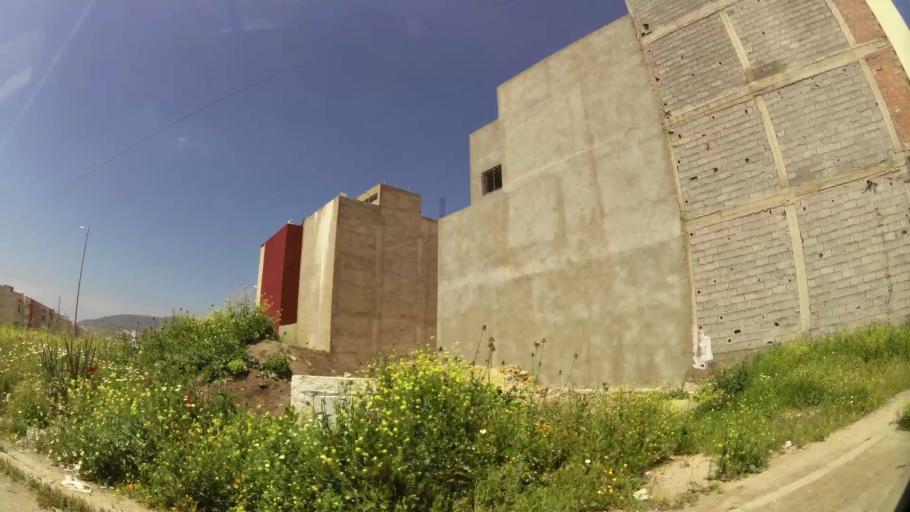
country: MA
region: Fes-Boulemane
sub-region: Fes
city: Fes
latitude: 34.0237
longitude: -5.0429
